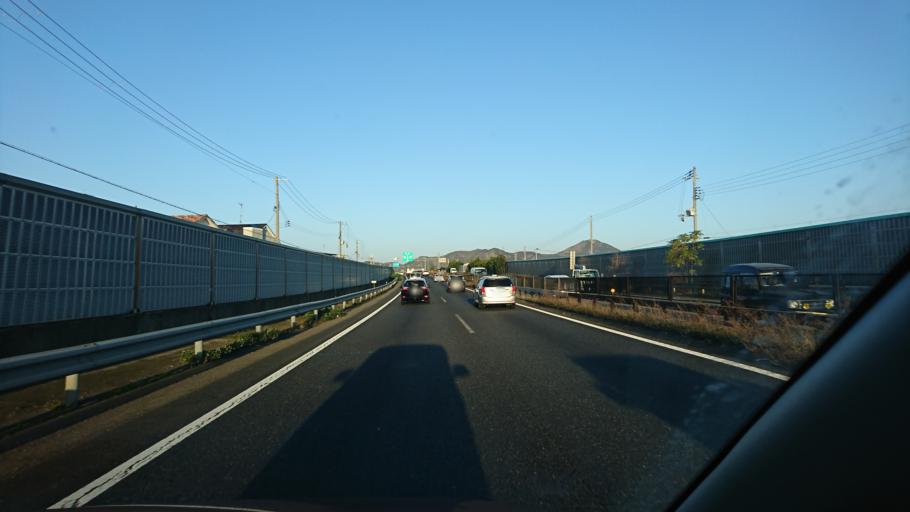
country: JP
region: Hyogo
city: Kakogawacho-honmachi
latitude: 34.7850
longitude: 134.8265
